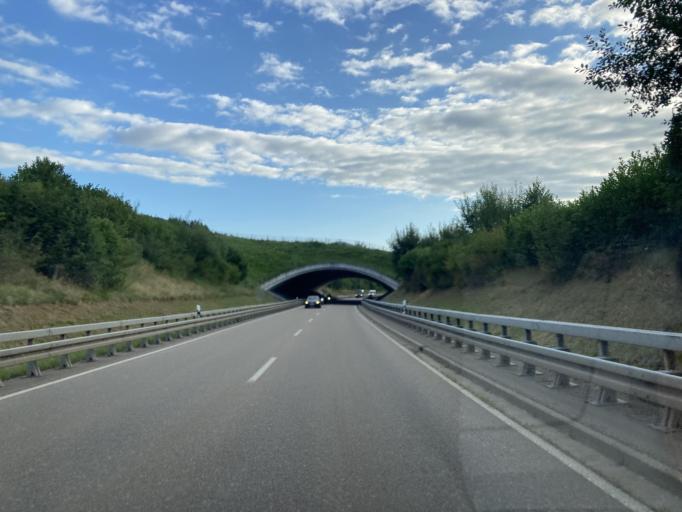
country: DE
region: Baden-Wuerttemberg
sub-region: Freiburg Region
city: Elzach
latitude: 48.1768
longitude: 8.0781
